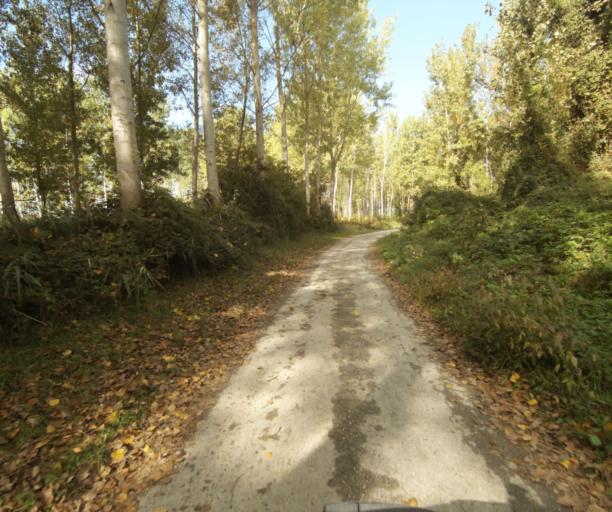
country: FR
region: Midi-Pyrenees
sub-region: Departement du Tarn-et-Garonne
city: Finhan
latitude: 43.9116
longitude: 1.2047
